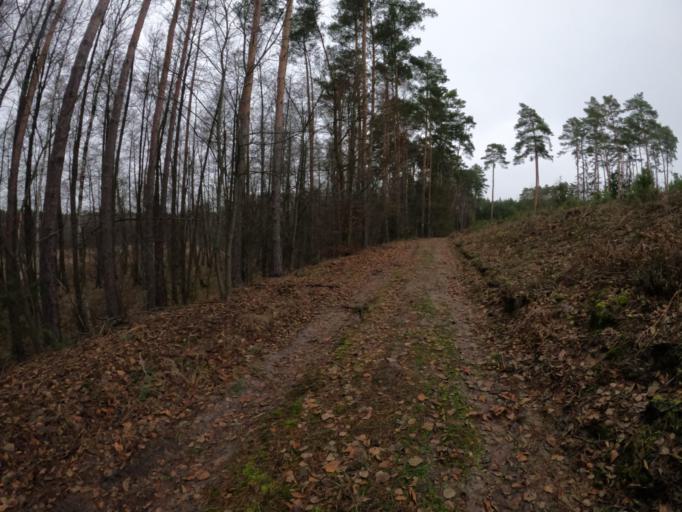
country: PL
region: West Pomeranian Voivodeship
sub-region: Powiat mysliborski
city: Debno
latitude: 52.7326
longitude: 14.7560
